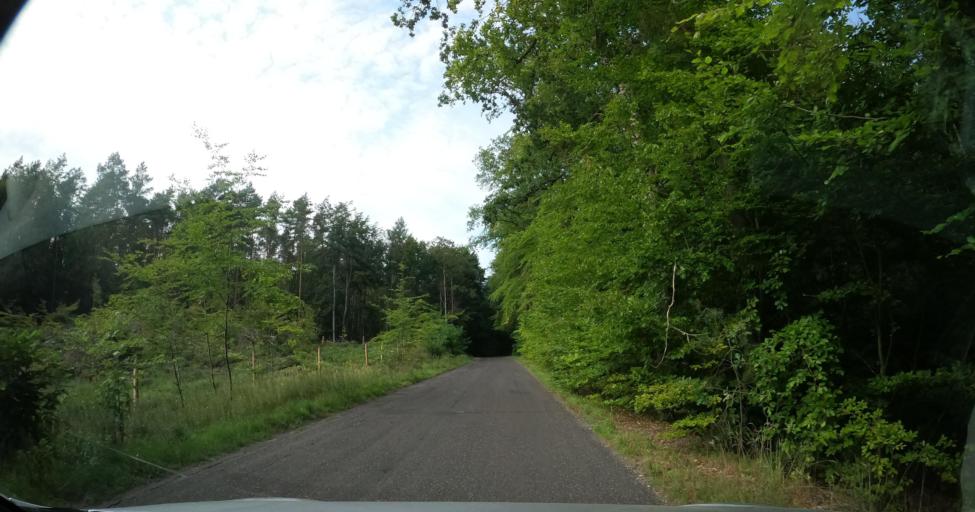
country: PL
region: West Pomeranian Voivodeship
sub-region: Powiat goleniowski
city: Goleniow
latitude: 53.5263
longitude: 14.8519
